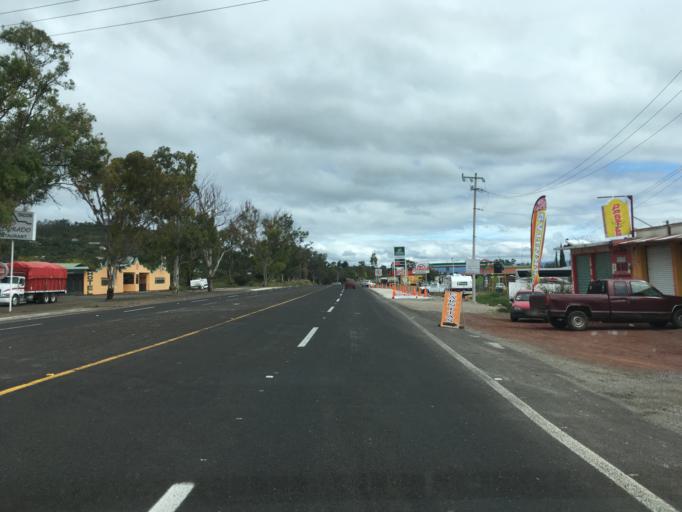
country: MX
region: Hidalgo
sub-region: Atotonilco el Grande
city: Santa Maria Amajac
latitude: 20.4008
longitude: -98.7163
